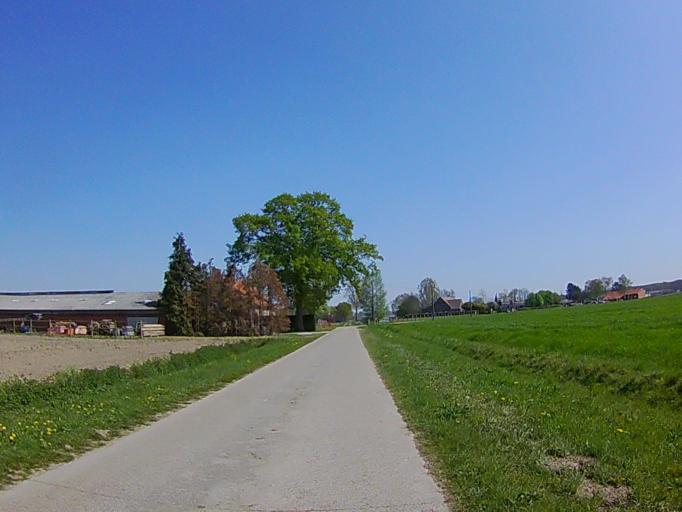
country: BE
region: Flanders
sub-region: Provincie Antwerpen
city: Hoogstraten
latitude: 51.3758
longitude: 4.7092
